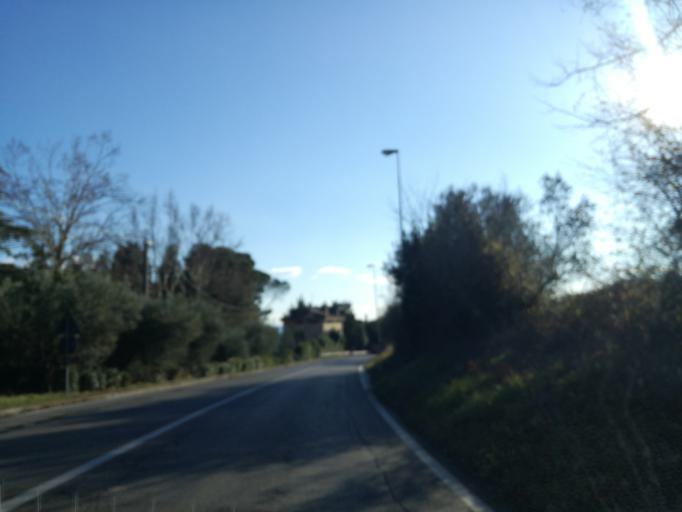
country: IT
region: Umbria
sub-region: Provincia di Perugia
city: Perugia
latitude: 43.0831
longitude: 12.4009
